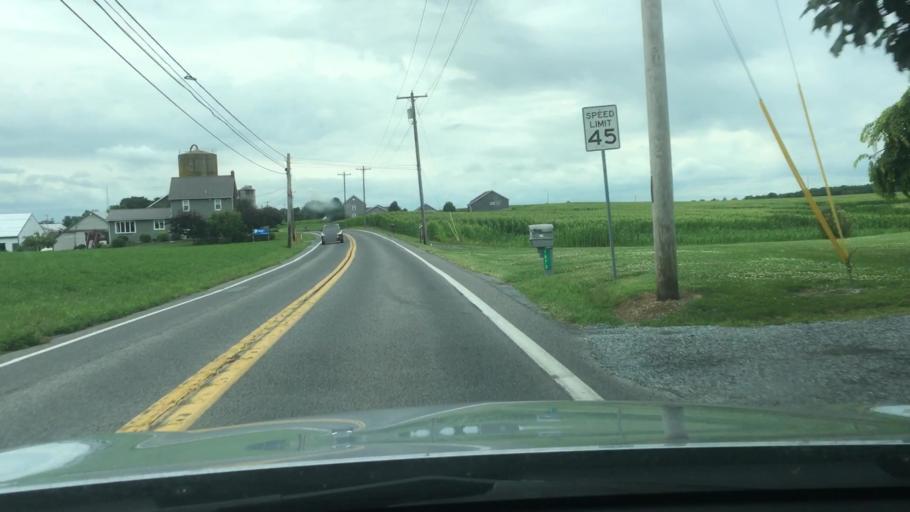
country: US
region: Pennsylvania
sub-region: Franklin County
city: Chambersburg
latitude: 39.8931
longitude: -77.7238
